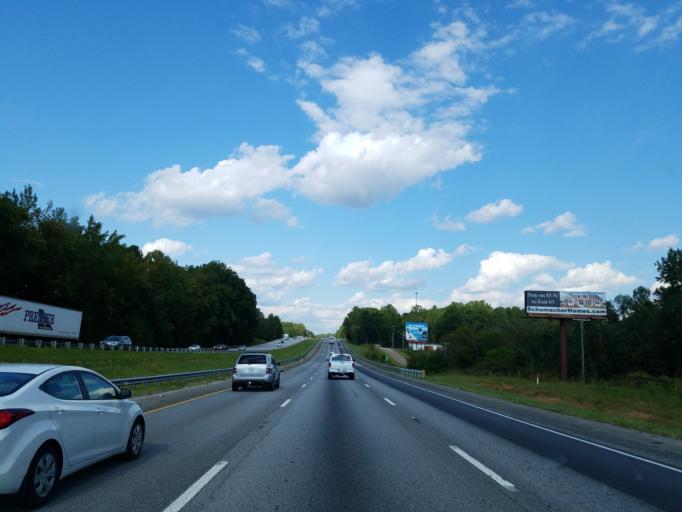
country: US
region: South Carolina
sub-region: Anderson County
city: Northlake
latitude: 34.5893
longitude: -82.6732
